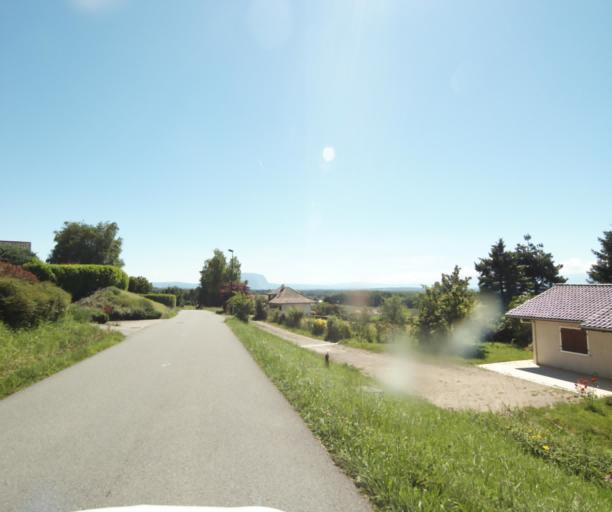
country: FR
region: Rhone-Alpes
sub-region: Departement de la Haute-Savoie
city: Loisin
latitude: 46.2768
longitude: 6.3161
